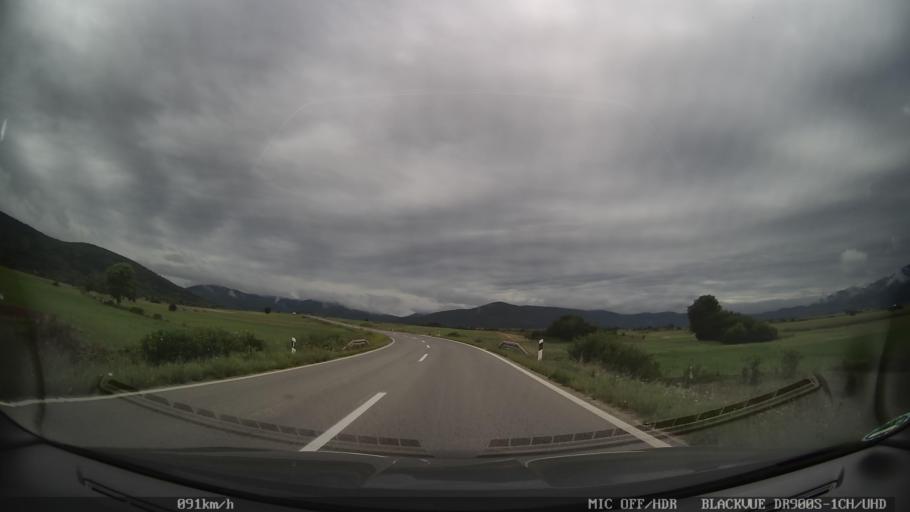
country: HR
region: Licko-Senjska
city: Otocac
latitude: 44.8558
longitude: 15.2808
